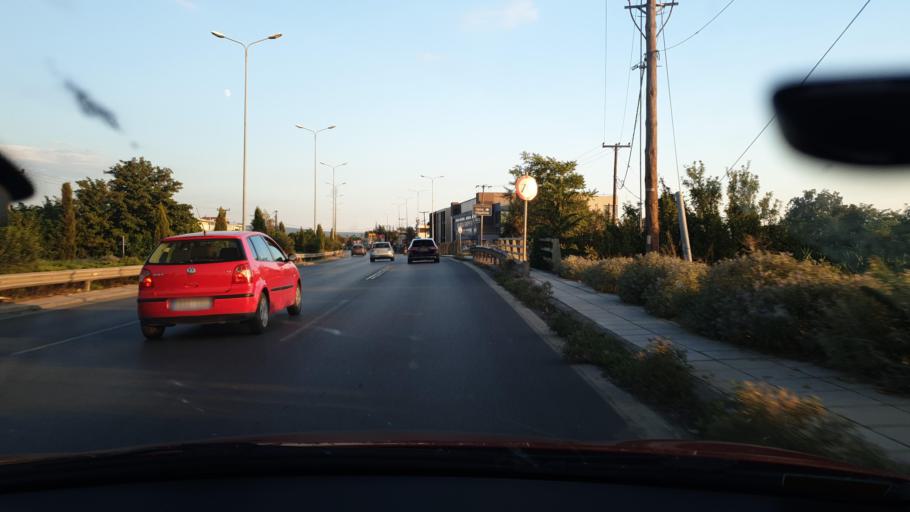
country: GR
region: Central Macedonia
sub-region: Nomos Thessalonikis
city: Thermi
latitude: 40.5462
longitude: 22.9843
